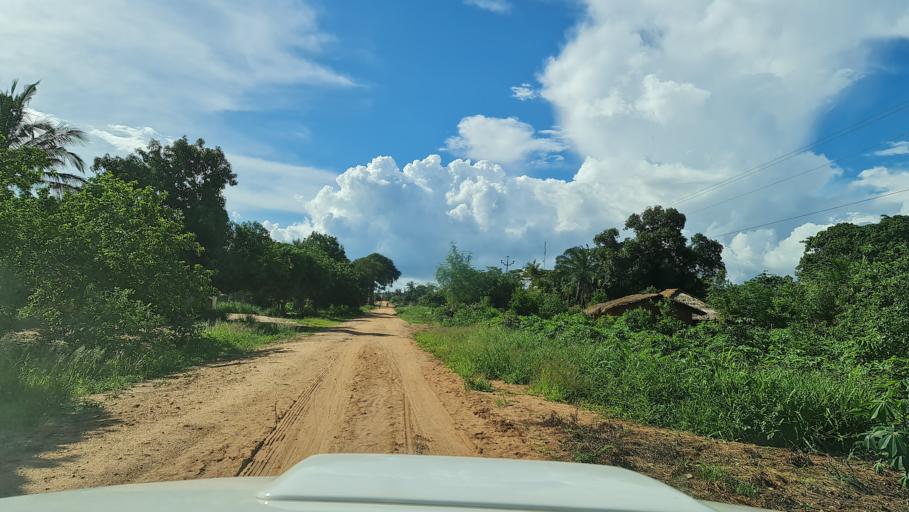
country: MZ
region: Nampula
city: Ilha de Mocambique
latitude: -15.2924
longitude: 40.1183
